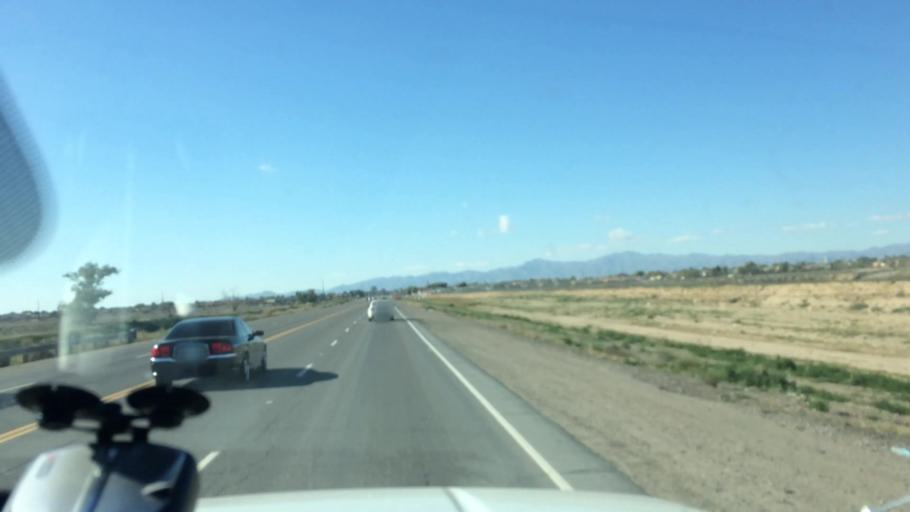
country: US
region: Arizona
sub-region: Maricopa County
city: Litchfield Park
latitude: 33.5079
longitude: -112.3165
